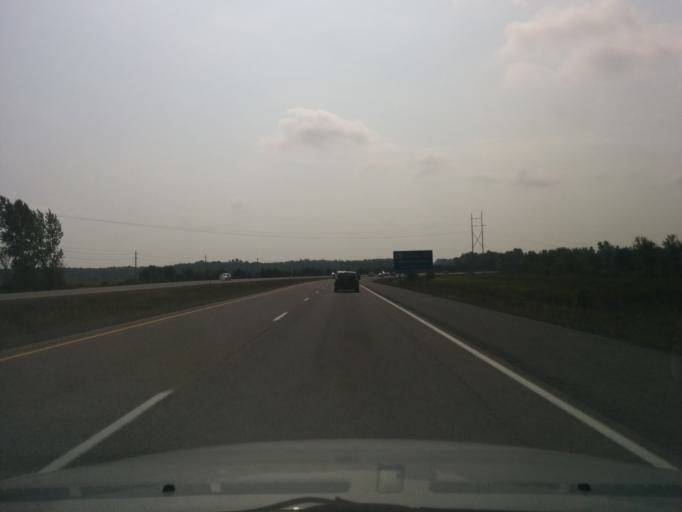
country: CA
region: Ontario
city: Bells Corners
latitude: 45.3039
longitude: -75.7944
